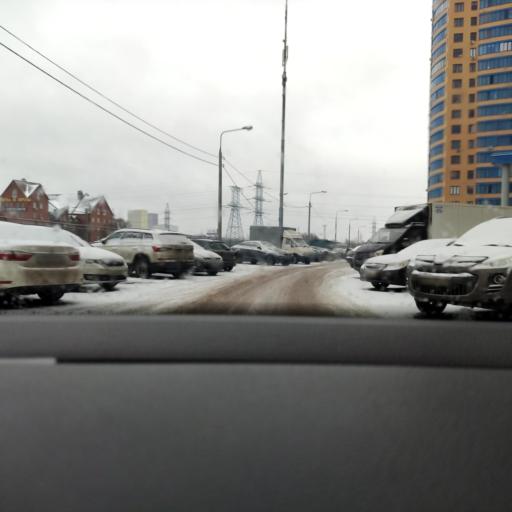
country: RU
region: Moscow
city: Ivanovskoye
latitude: 55.7749
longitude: 37.8468
